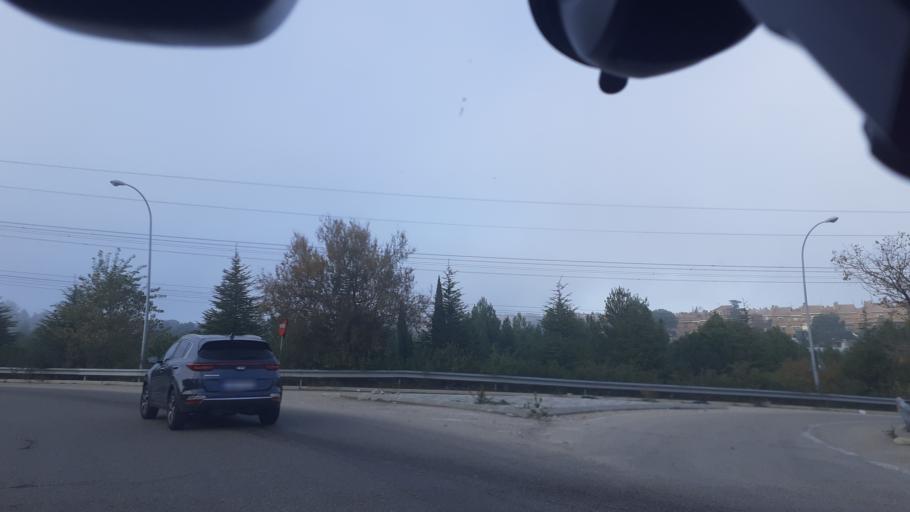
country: ES
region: Madrid
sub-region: Provincia de Madrid
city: Coslada
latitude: 40.4117
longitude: -3.5514
